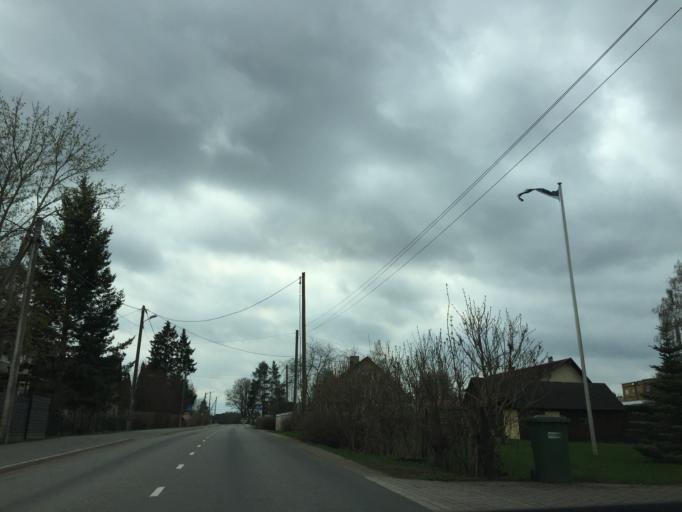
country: EE
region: Tartu
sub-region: Noo vald
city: Noo
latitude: 58.2733
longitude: 26.5332
